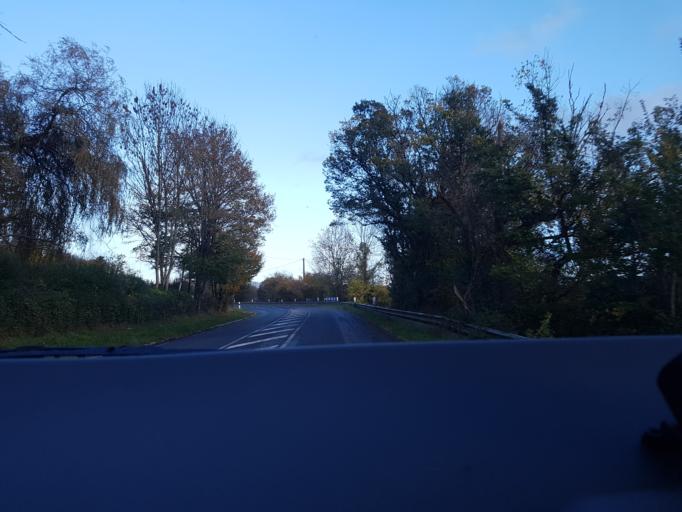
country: FR
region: Lower Normandy
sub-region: Departement du Calvados
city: Dozule
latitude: 49.2500
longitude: 0.0297
